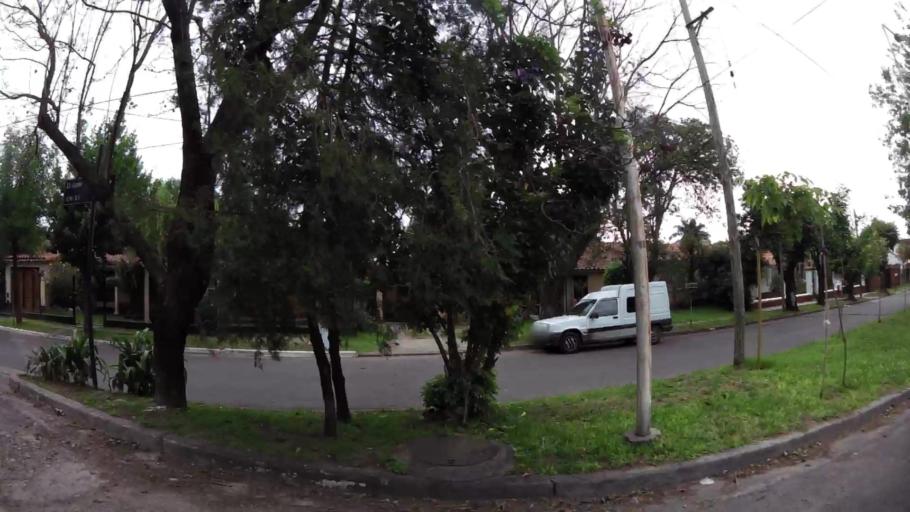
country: AR
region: Buenos Aires
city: San Justo
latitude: -34.7201
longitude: -58.5332
